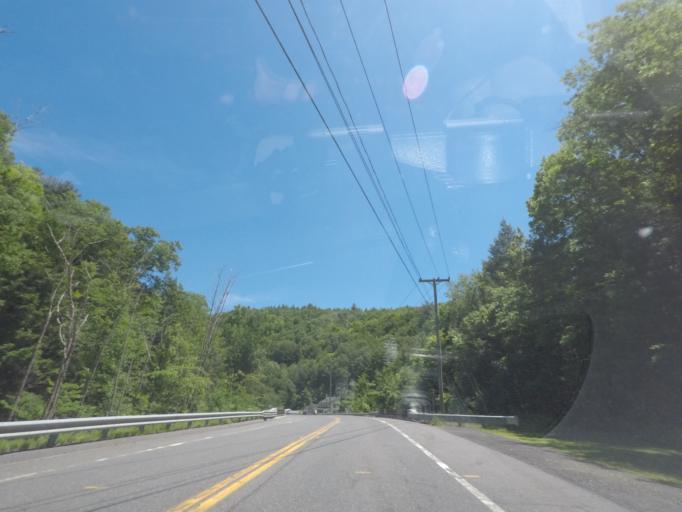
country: US
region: Massachusetts
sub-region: Berkshire County
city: Becket
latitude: 42.2683
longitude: -73.0128
